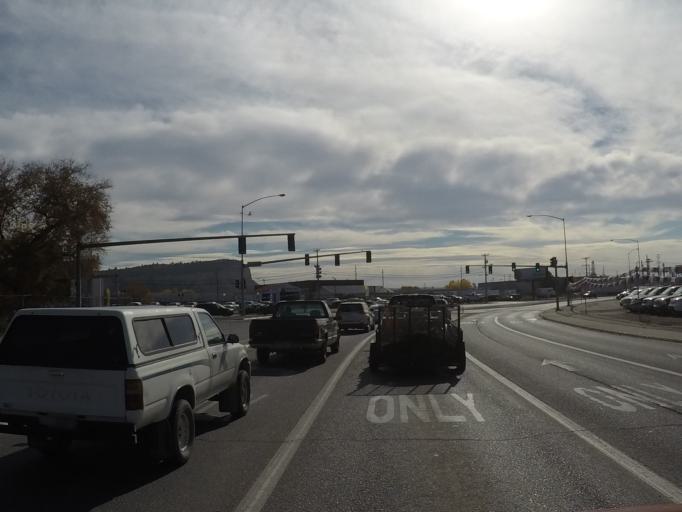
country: US
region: Montana
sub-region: Yellowstone County
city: Billings
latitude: 45.7949
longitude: -108.4814
